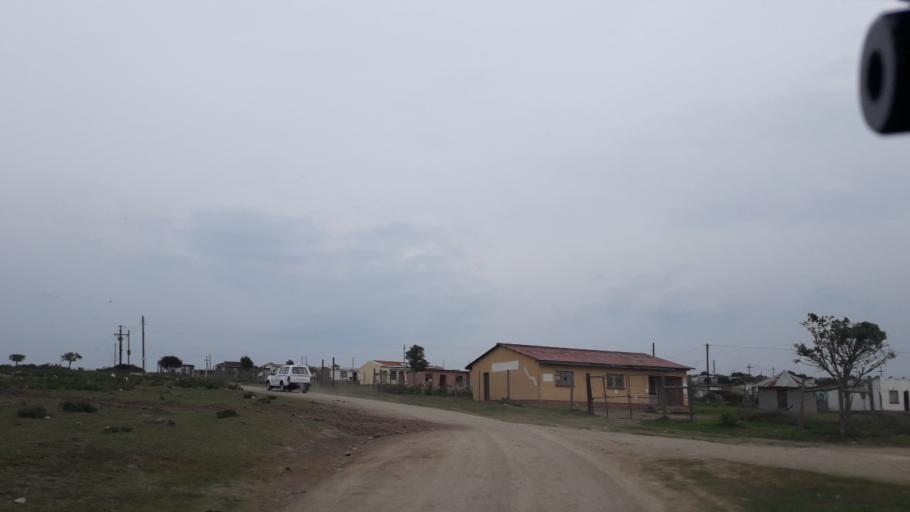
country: ZA
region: Eastern Cape
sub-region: Buffalo City Metropolitan Municipality
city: Bhisho
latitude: -32.8337
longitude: 27.3728
